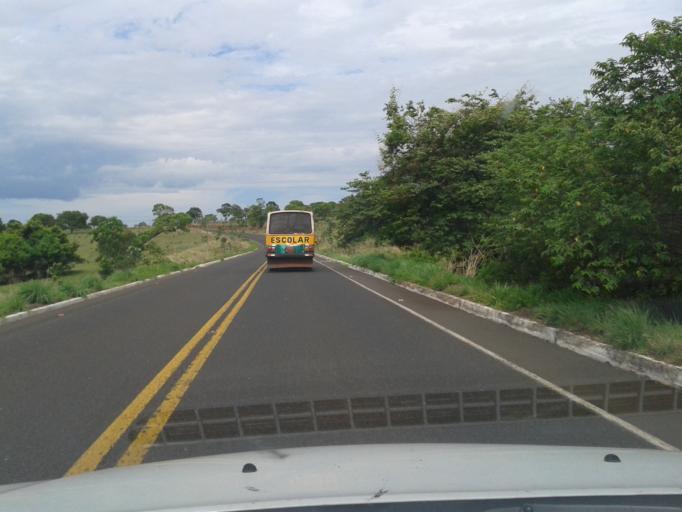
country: BR
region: Minas Gerais
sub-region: Iturama
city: Iturama
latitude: -19.5726
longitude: -49.9522
